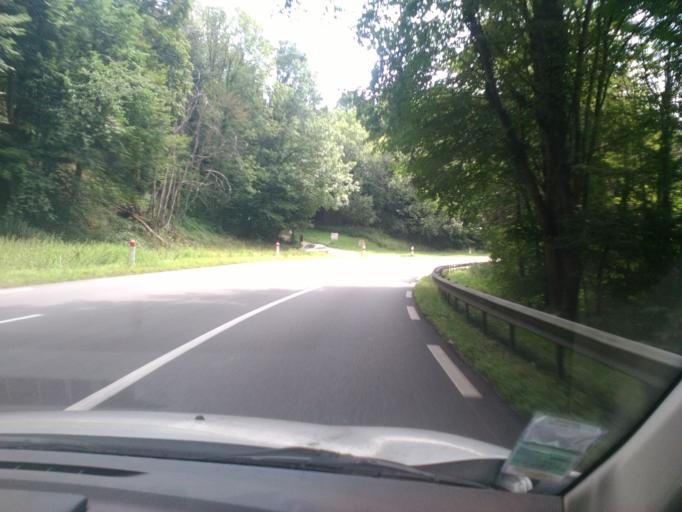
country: FR
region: Alsace
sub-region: Departement du Haut-Rhin
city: Lapoutroie
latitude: 48.1634
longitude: 7.1621
